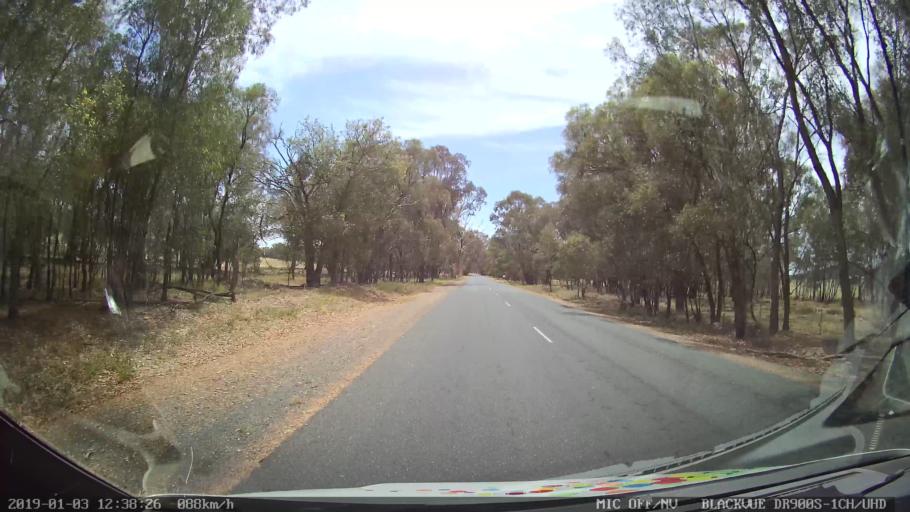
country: AU
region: New South Wales
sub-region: Weddin
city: Grenfell
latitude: -33.8334
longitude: 148.1955
